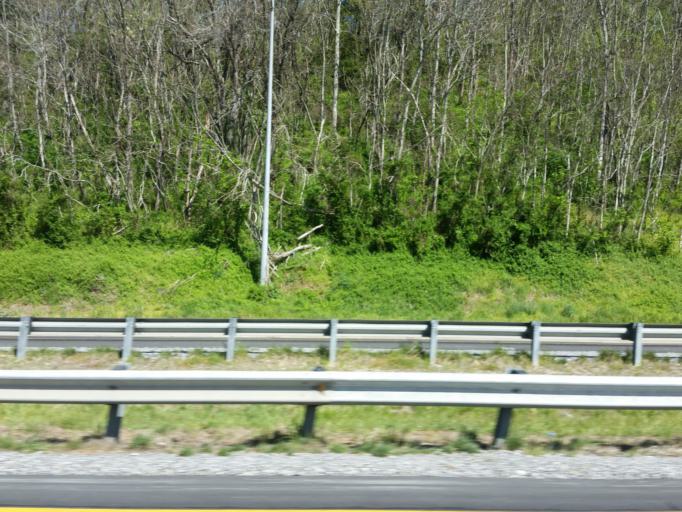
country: US
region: North Carolina
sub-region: Buncombe County
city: Asheville
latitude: 35.6071
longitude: -82.5773
